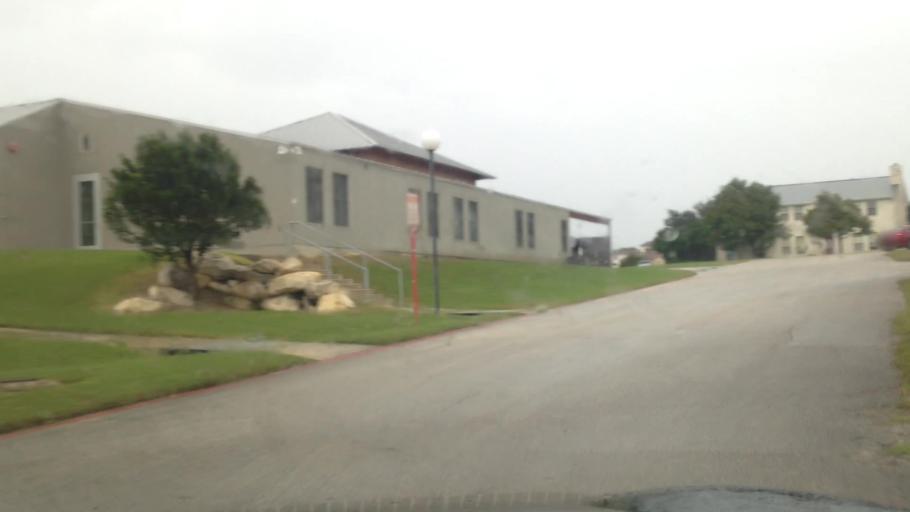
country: US
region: Texas
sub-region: Bexar County
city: Cross Mountain
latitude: 29.6396
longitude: -98.6044
